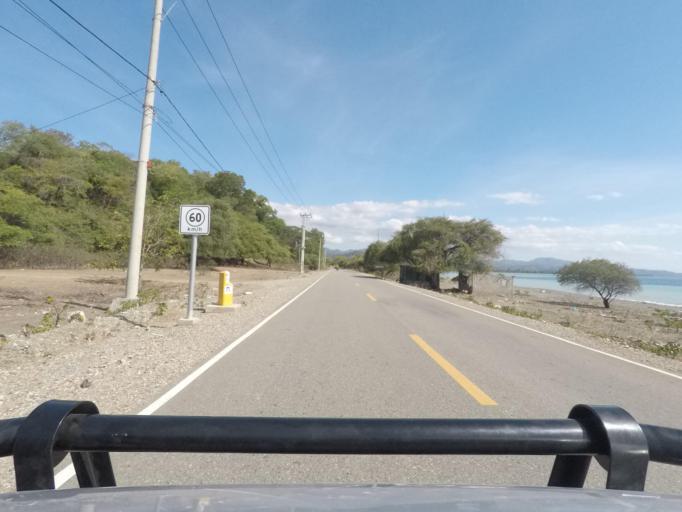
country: ID
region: East Nusa Tenggara
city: Atambua
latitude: -8.9340
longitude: 124.9802
